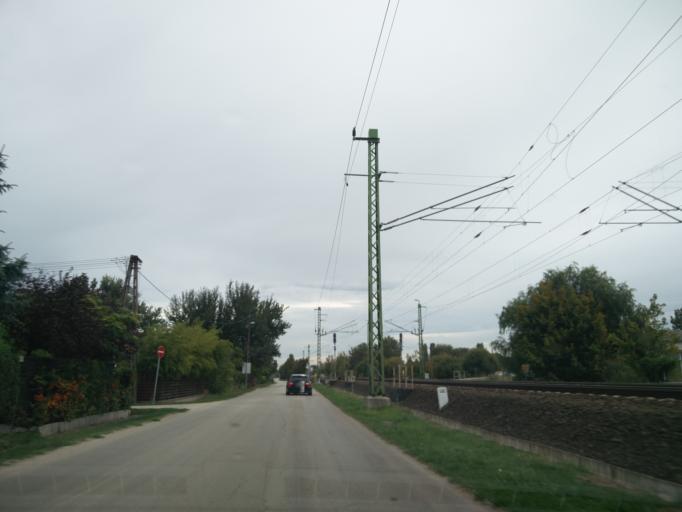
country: HU
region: Fejer
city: Gardony
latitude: 47.2093
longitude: 18.6305
